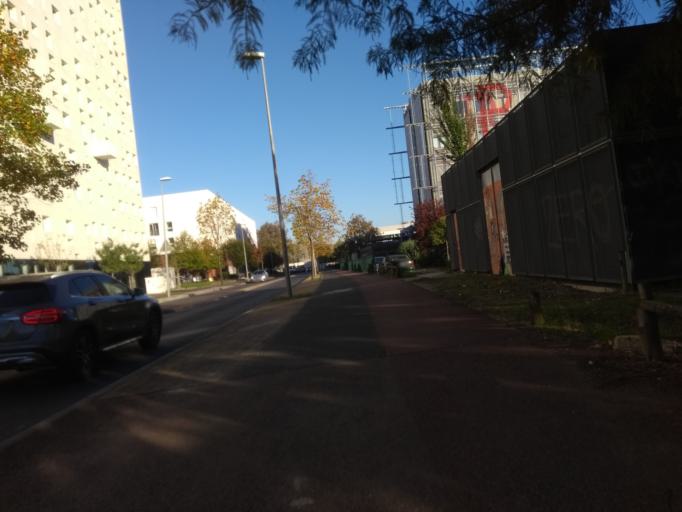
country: FR
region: Aquitaine
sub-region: Departement de la Gironde
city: Talence
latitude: 44.8011
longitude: -0.6095
